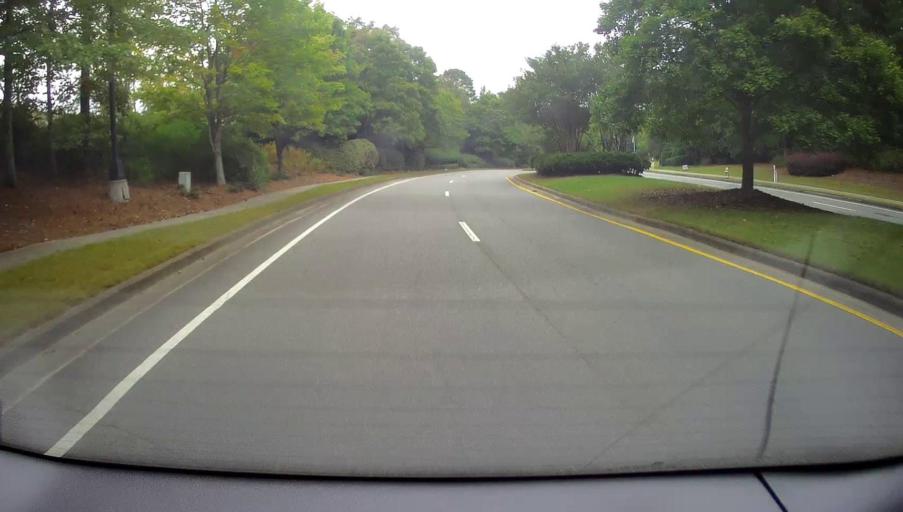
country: US
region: Georgia
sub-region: Fulton County
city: Alpharetta
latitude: 34.1022
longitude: -84.2660
